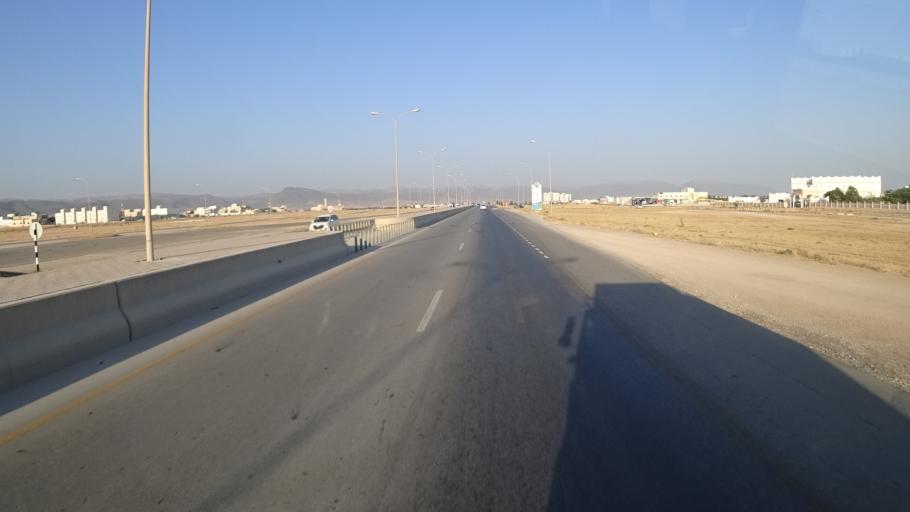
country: OM
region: Zufar
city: Salalah
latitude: 17.0917
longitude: 54.1402
